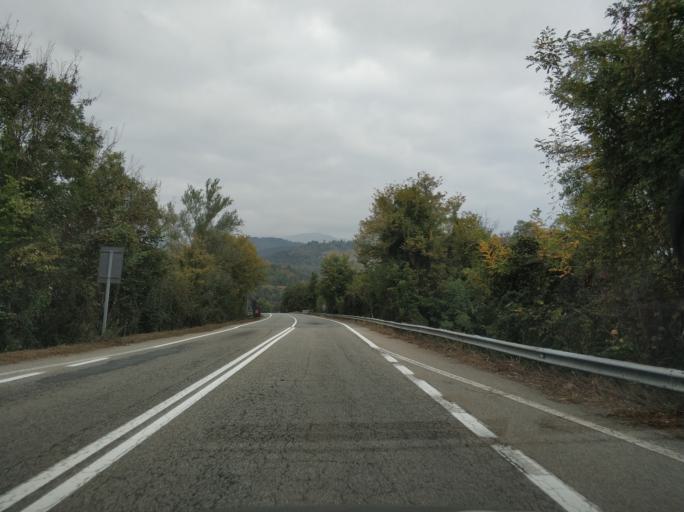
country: IT
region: Piedmont
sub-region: Provincia di Torino
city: Baldissero Canavese
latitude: 45.4074
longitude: 7.7555
